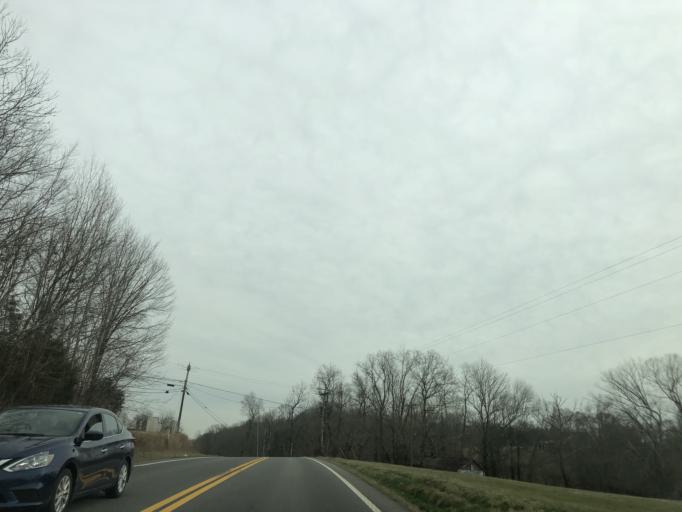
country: US
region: Tennessee
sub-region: Robertson County
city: Greenbrier
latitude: 36.4784
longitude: -86.7691
